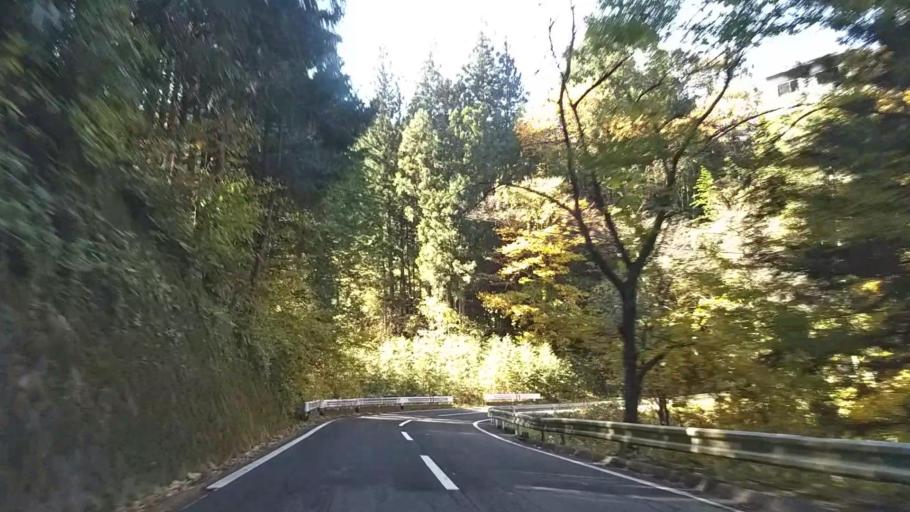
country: JP
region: Yamanashi
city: Otsuki
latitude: 35.7468
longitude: 138.9609
